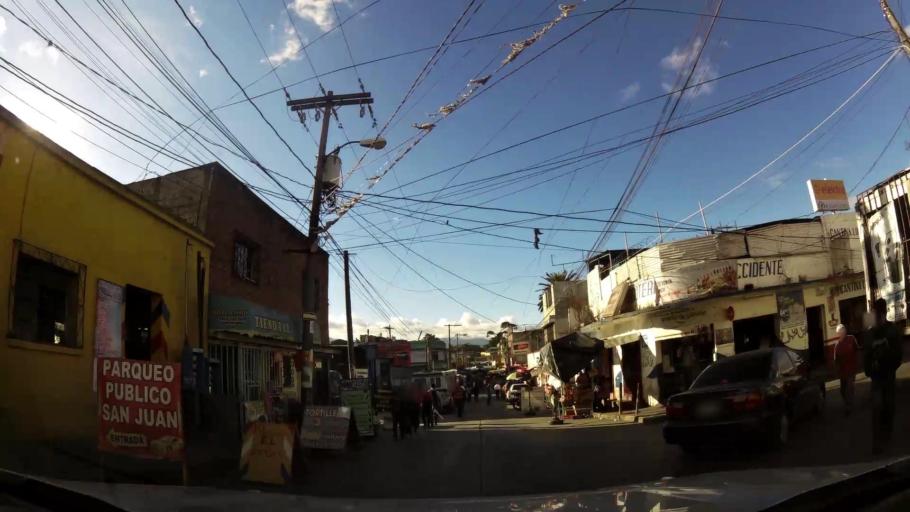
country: GT
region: Guatemala
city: Guatemala City
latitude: 14.6141
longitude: -90.5374
